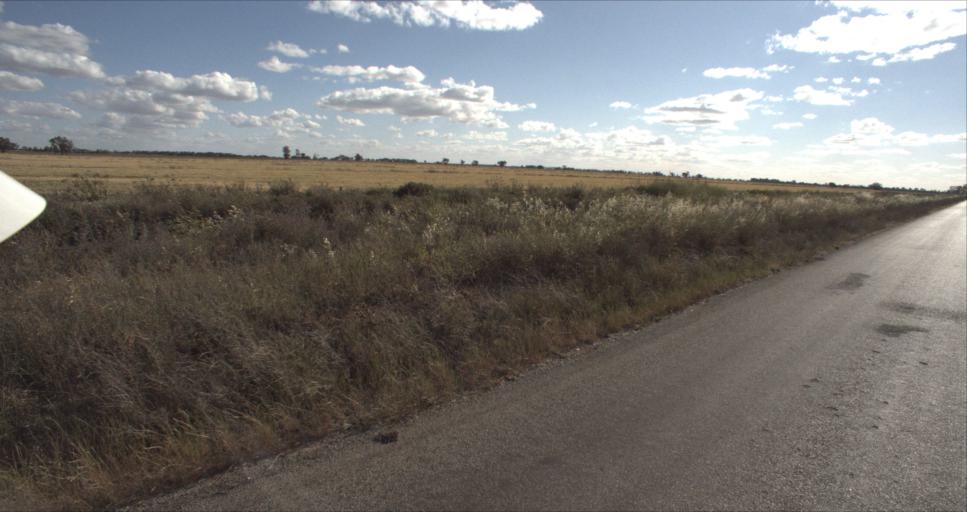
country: AU
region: New South Wales
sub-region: Leeton
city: Leeton
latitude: -34.4442
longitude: 146.2554
